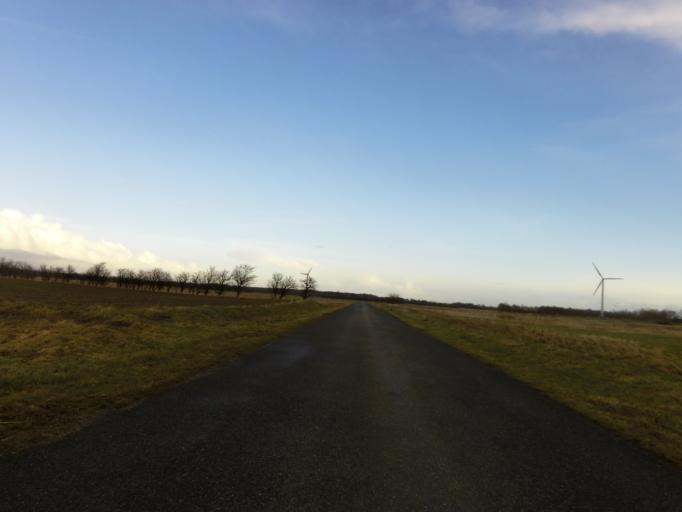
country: DK
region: South Denmark
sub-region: Tonder Kommune
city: Toftlund
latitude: 55.2406
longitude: 9.0671
